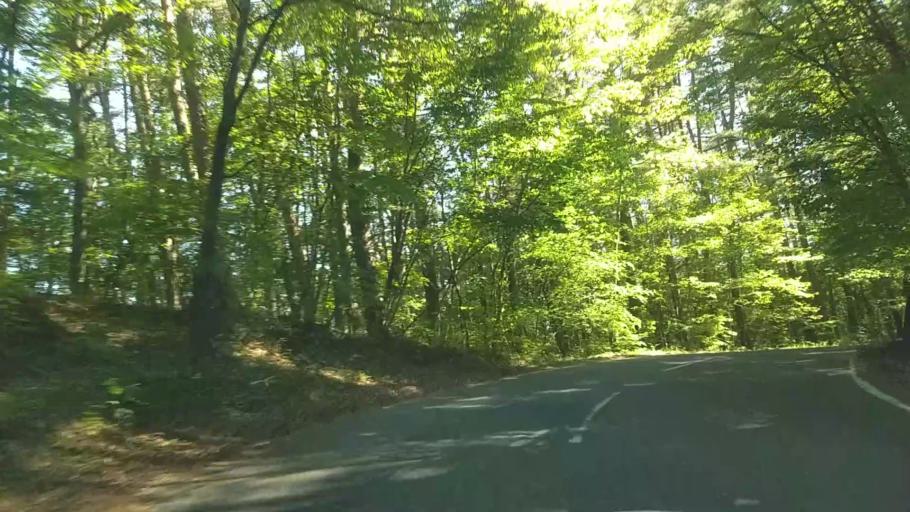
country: JP
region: Yamanashi
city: Nirasaki
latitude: 35.8900
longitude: 138.3923
